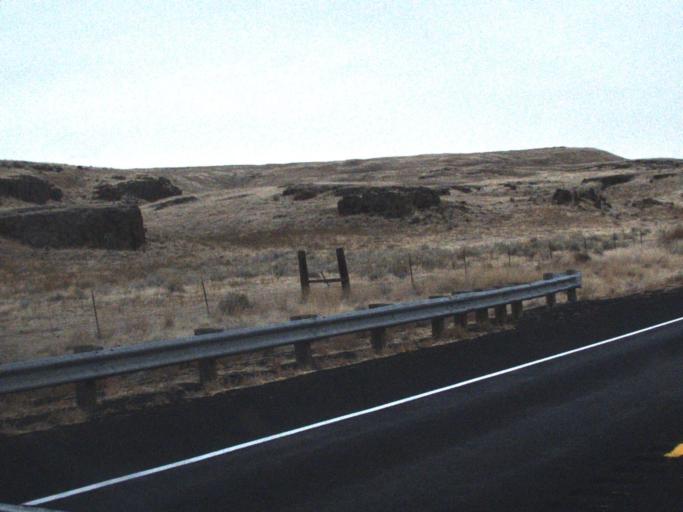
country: US
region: Washington
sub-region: Adams County
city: Ritzville
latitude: 46.7732
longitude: -118.1086
